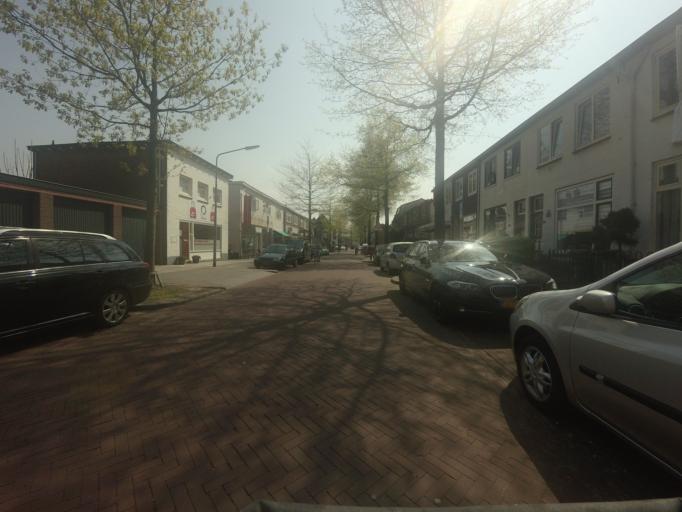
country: NL
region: North Holland
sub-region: Gemeente Hilversum
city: Hilversum
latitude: 52.2169
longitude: 5.1675
